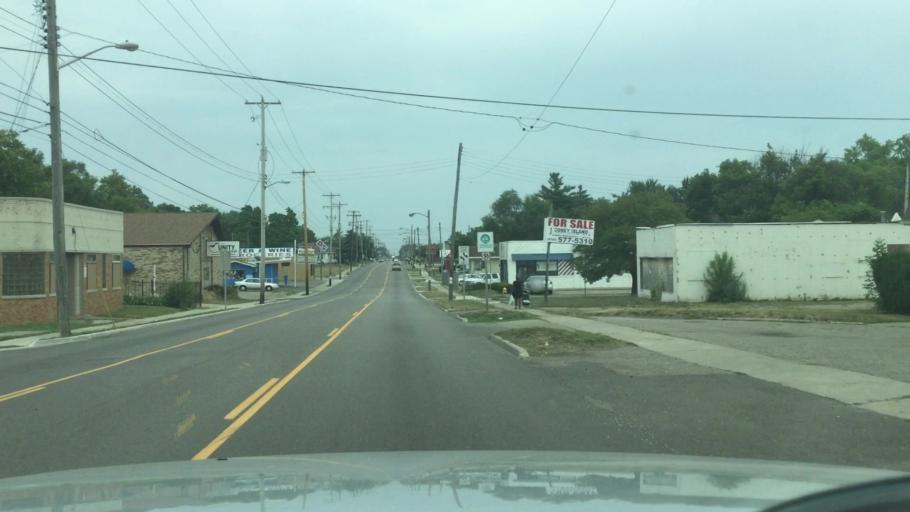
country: US
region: Michigan
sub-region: Genesee County
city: Flint
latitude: 42.9823
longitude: -83.6929
